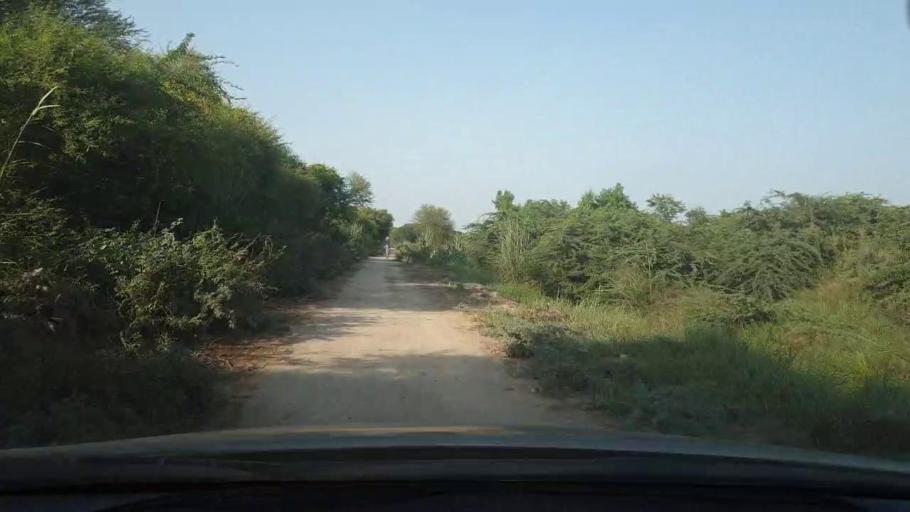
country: PK
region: Sindh
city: Naukot
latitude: 24.7820
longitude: 69.2345
